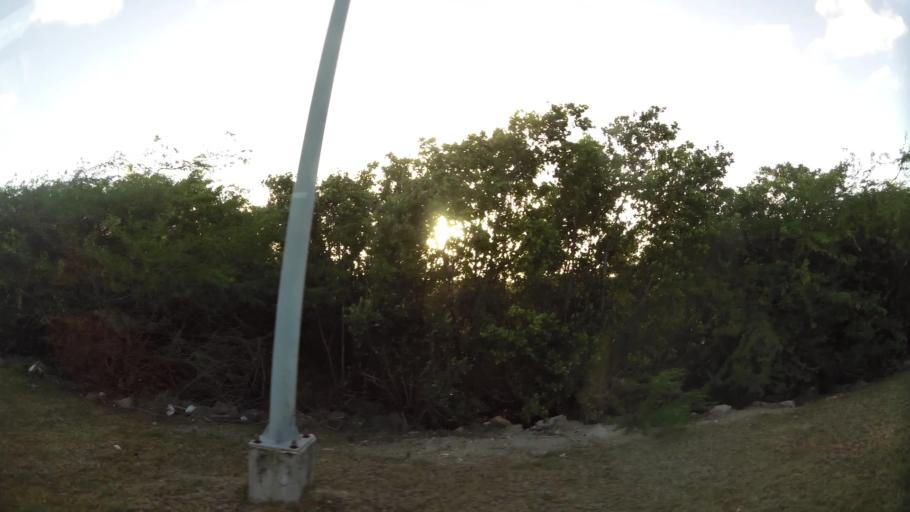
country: AG
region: Saint George
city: Piggotts
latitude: 17.1618
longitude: -61.7983
